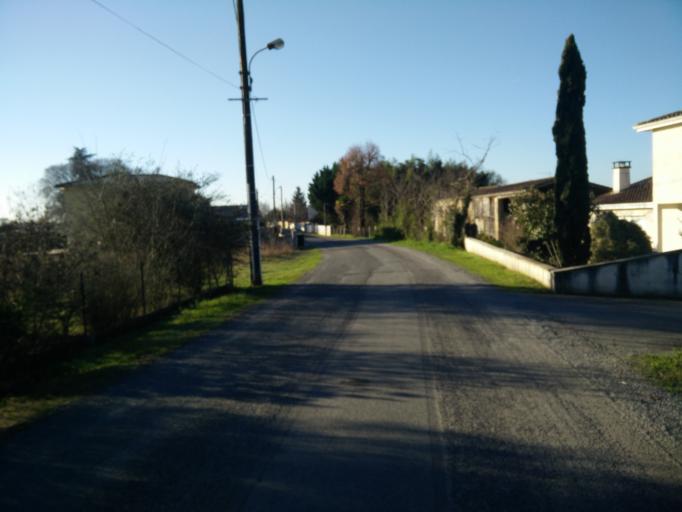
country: FR
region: Aquitaine
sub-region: Departement de la Gironde
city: Galgon
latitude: 44.9585
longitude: -0.2335
